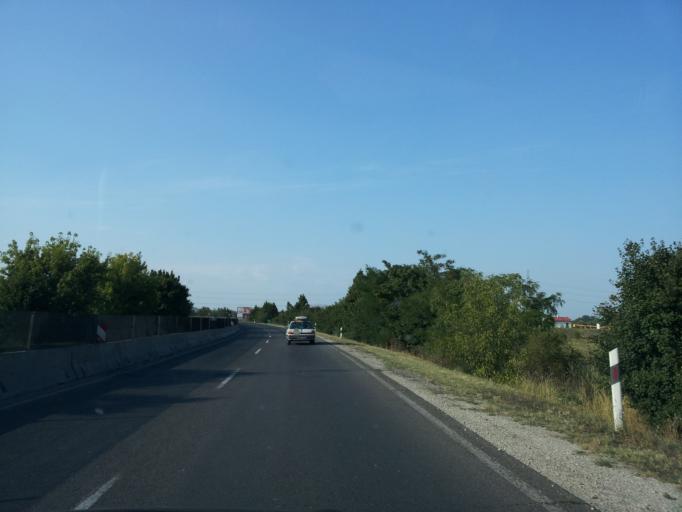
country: HU
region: Pest
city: Budakalasz
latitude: 47.6316
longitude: 19.0704
